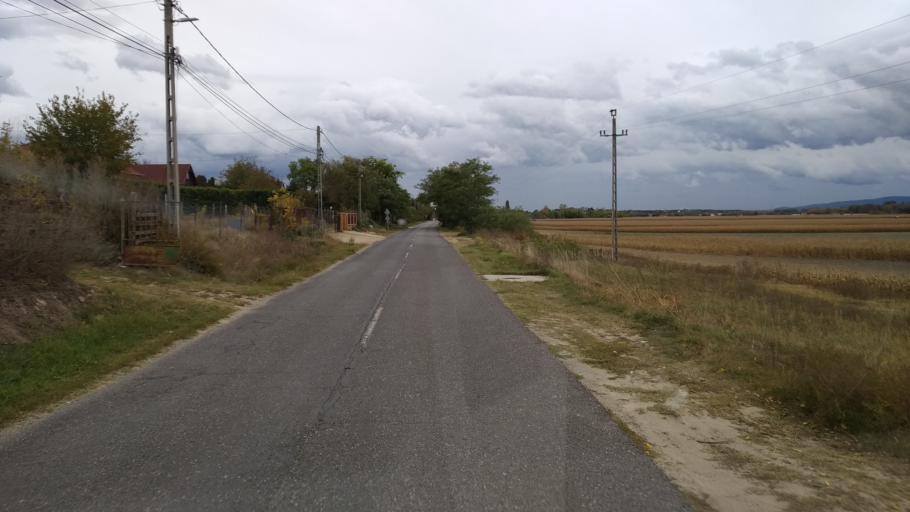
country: HU
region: Pest
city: Leanyfalu
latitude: 47.7115
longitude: 19.1062
